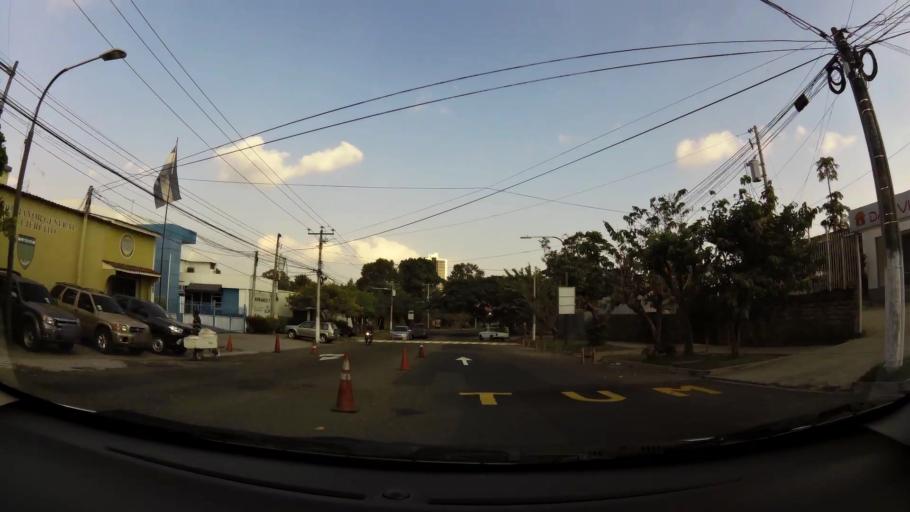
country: SV
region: La Libertad
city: Antiguo Cuscatlan
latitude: 13.6950
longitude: -89.2416
